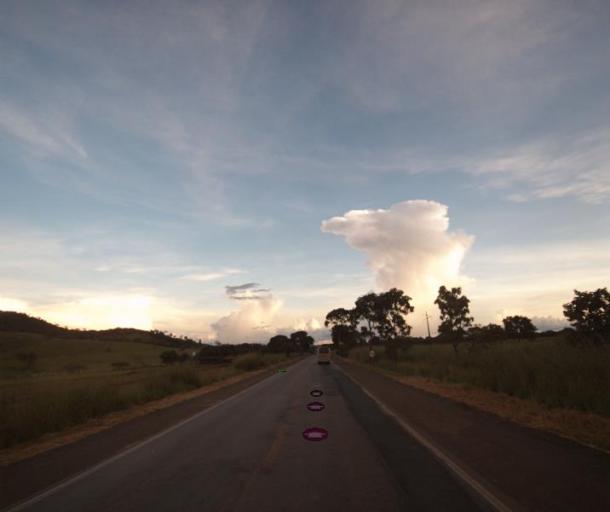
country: BR
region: Goias
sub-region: Uruacu
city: Uruacu
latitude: -14.4000
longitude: -49.1576
